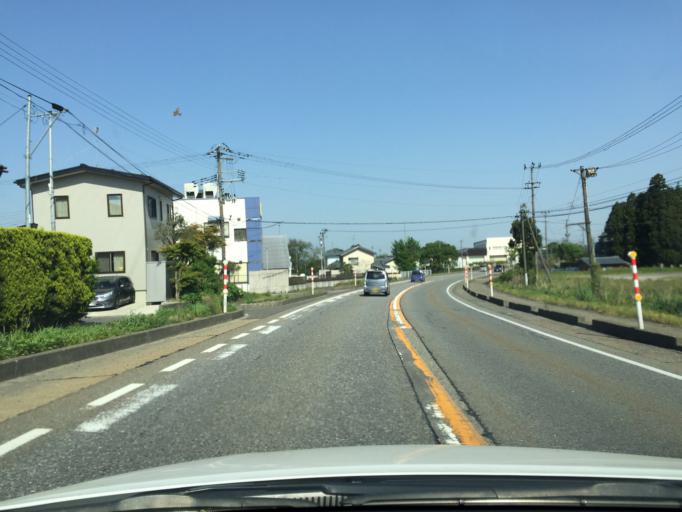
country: JP
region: Niigata
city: Gosen
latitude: 37.7488
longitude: 139.2529
